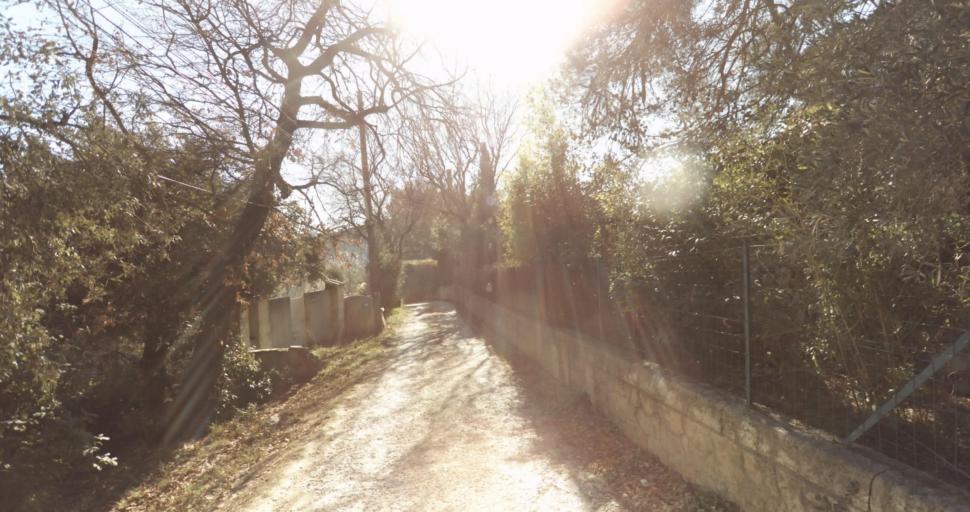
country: FR
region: Provence-Alpes-Cote d'Azur
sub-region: Departement des Bouches-du-Rhone
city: Peypin
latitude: 43.3882
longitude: 5.5704
